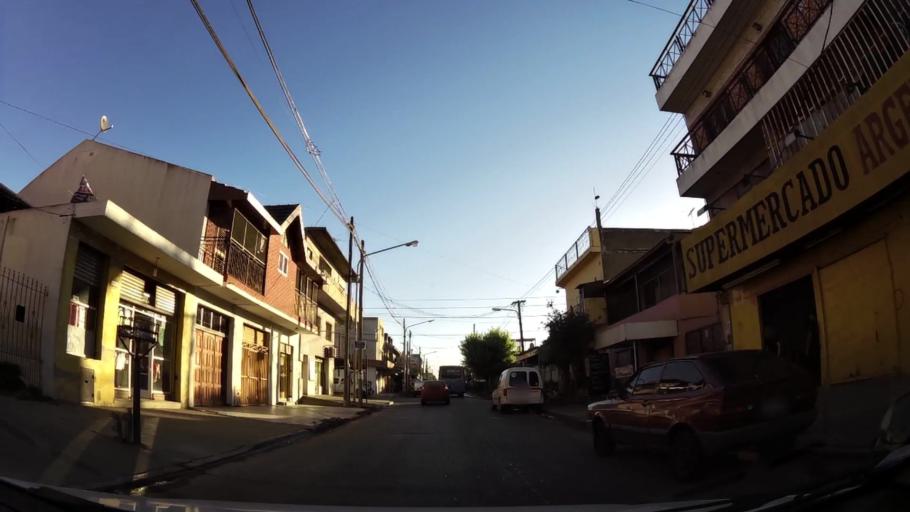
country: AR
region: Buenos Aires
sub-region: Partido de Moron
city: Moron
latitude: -34.7131
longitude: -58.6123
